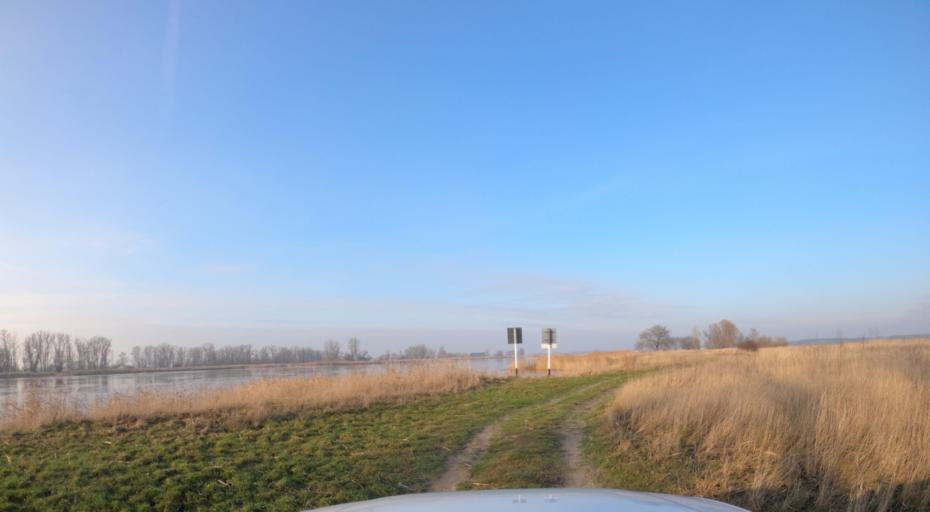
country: PL
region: Lubusz
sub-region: Powiat gorzowski
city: Kostrzyn nad Odra
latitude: 52.6024
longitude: 14.6073
